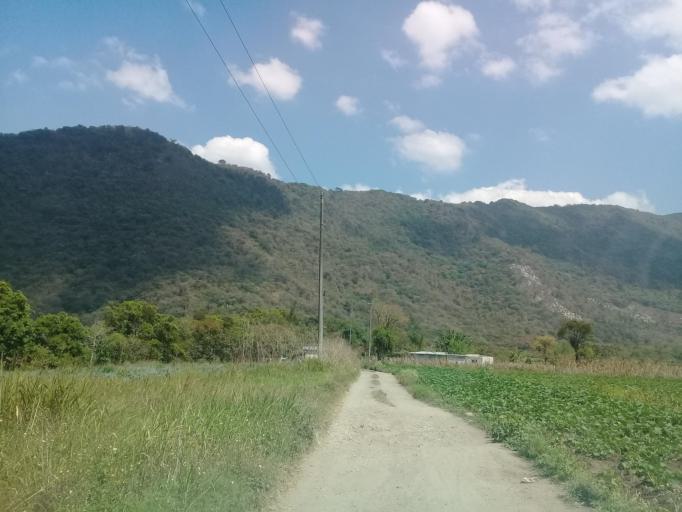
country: MX
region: Veracruz
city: Jalapilla
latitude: 18.8290
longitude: -97.0732
